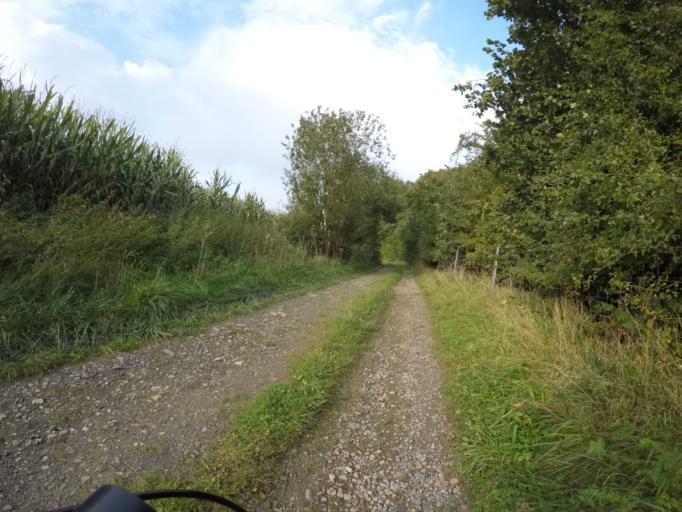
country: DE
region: North Rhine-Westphalia
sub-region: Regierungsbezirk Detmold
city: Herford
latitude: 52.1091
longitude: 8.6436
